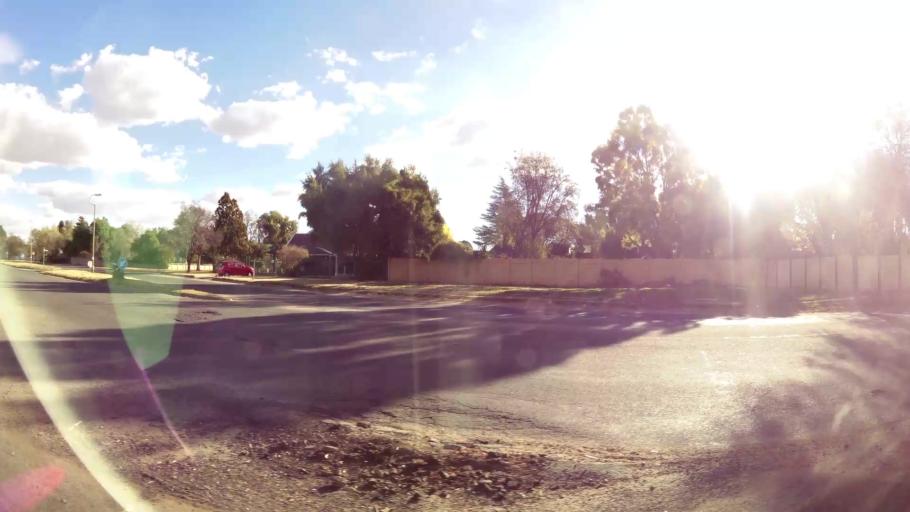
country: ZA
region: North-West
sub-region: Dr Kenneth Kaunda District Municipality
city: Klerksdorp
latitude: -26.8334
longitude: 26.6619
